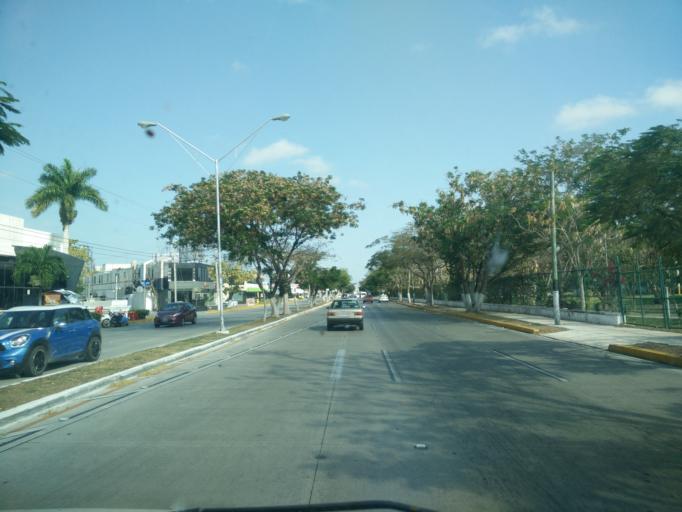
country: MX
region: Yucatan
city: Merida
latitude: 21.0146
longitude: -89.6148
